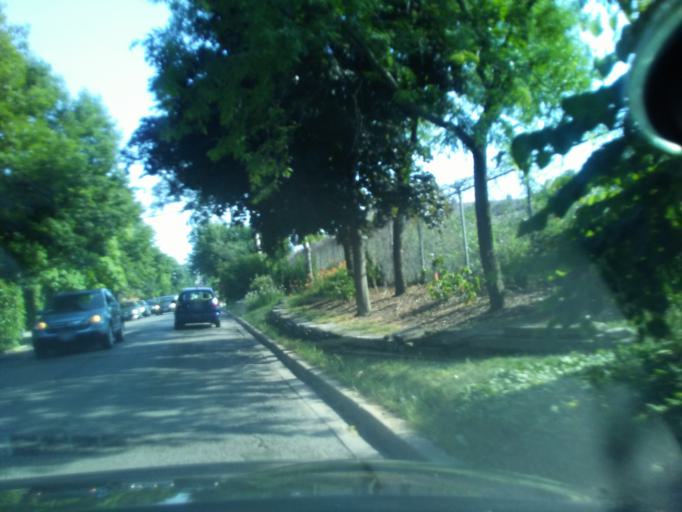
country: US
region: Illinois
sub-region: Cook County
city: Lincolnwood
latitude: 41.9741
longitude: -87.6745
